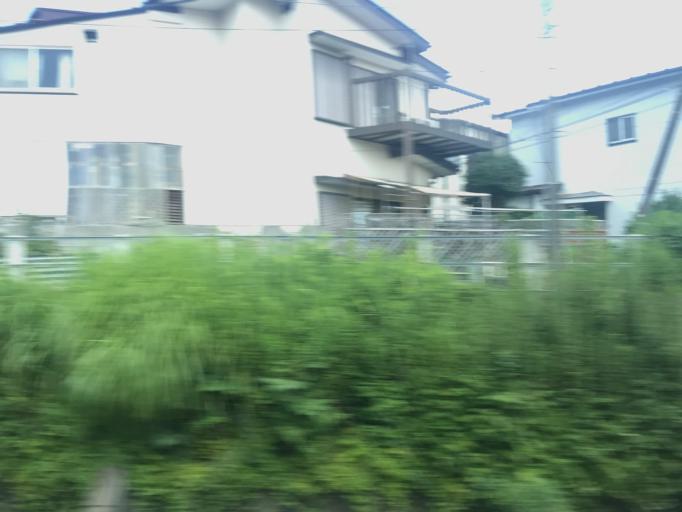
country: JP
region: Kanagawa
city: Fujisawa
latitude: 35.3689
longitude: 139.4730
